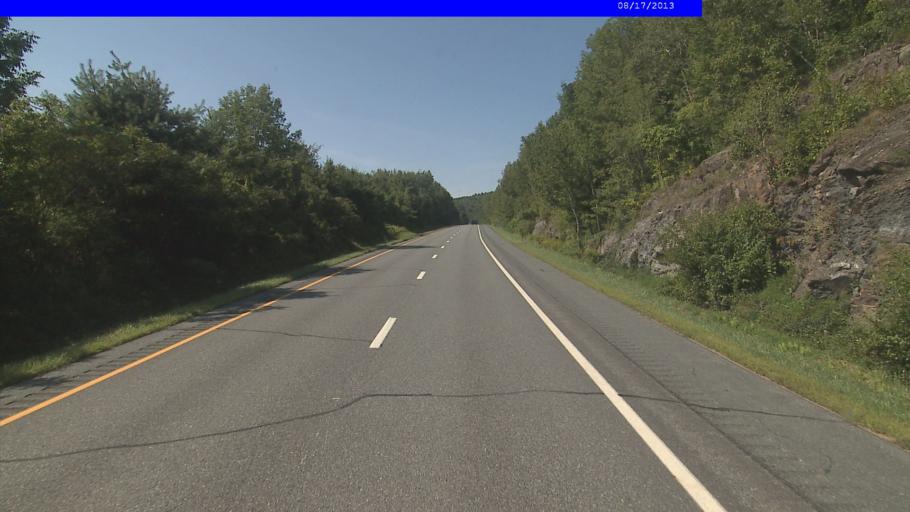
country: US
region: New Hampshire
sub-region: Sullivan County
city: Charlestown
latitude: 43.2538
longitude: -72.4415
